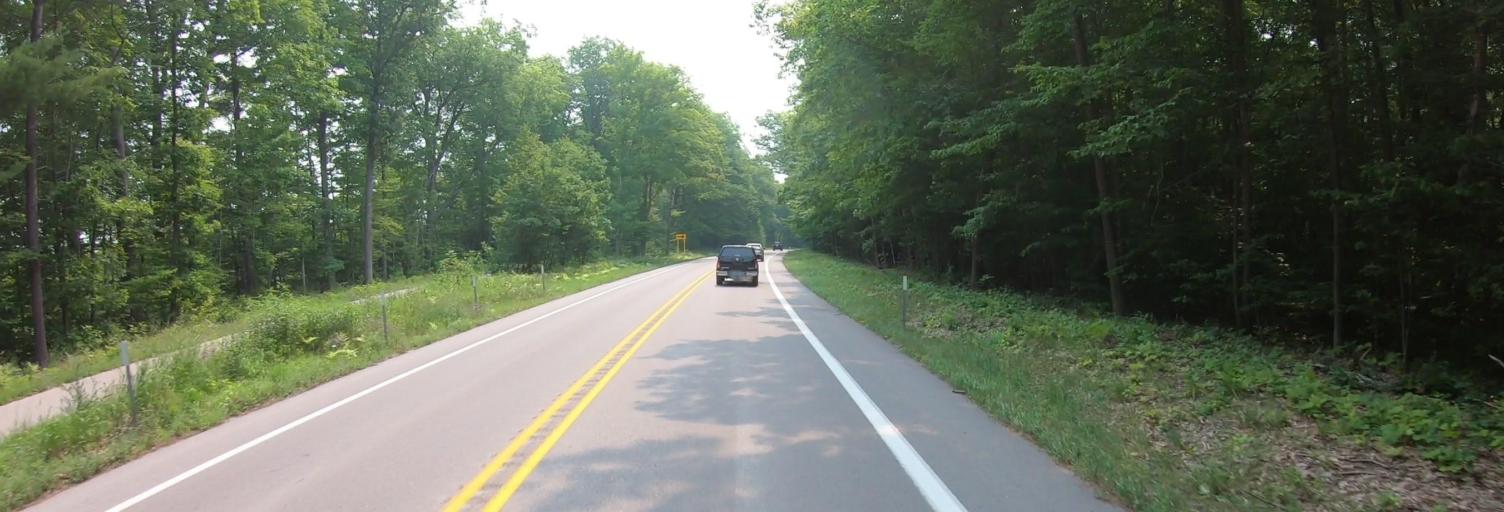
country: US
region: Michigan
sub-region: Leelanau County
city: Leland
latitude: 44.9314
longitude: -85.8877
